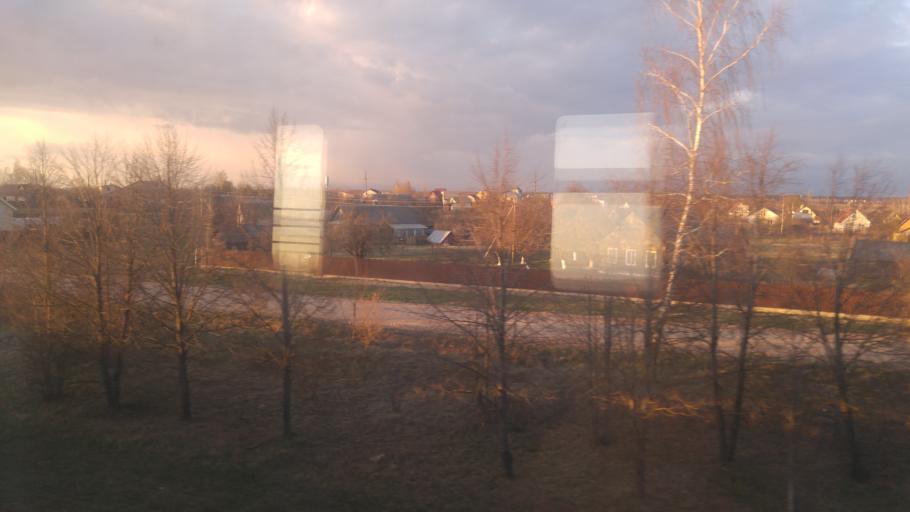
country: BY
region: Minsk
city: Rudzyensk
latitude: 53.6380
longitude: 27.7954
